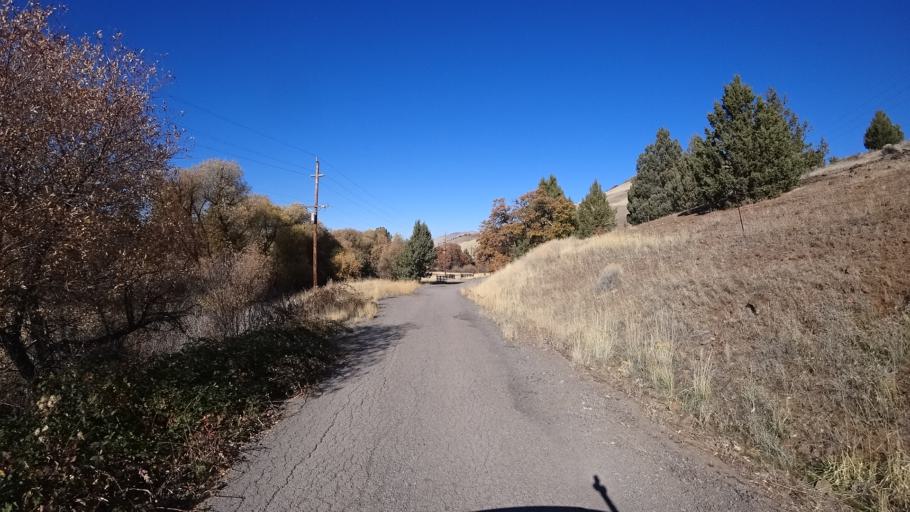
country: US
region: California
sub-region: Siskiyou County
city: Montague
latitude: 41.7907
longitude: -122.3604
